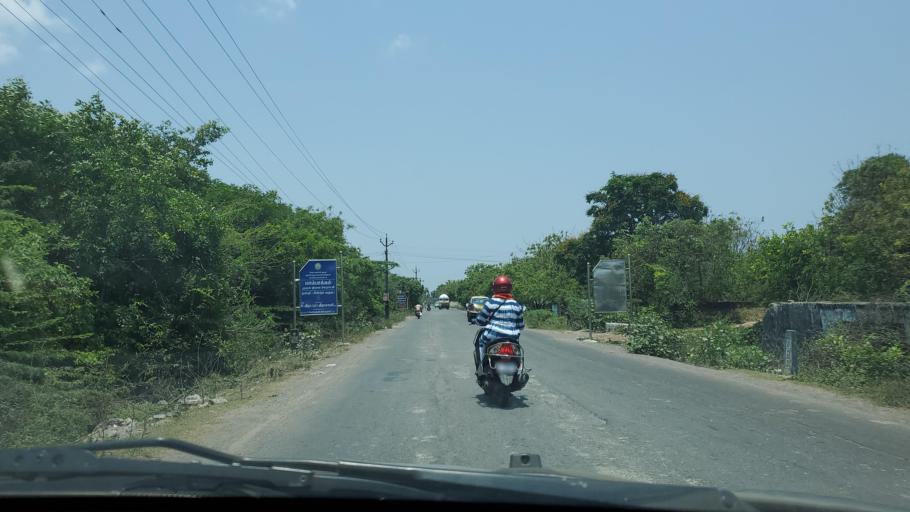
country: IN
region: Tamil Nadu
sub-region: Kancheepuram
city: Vengavasal
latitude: 12.8484
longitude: 80.1705
